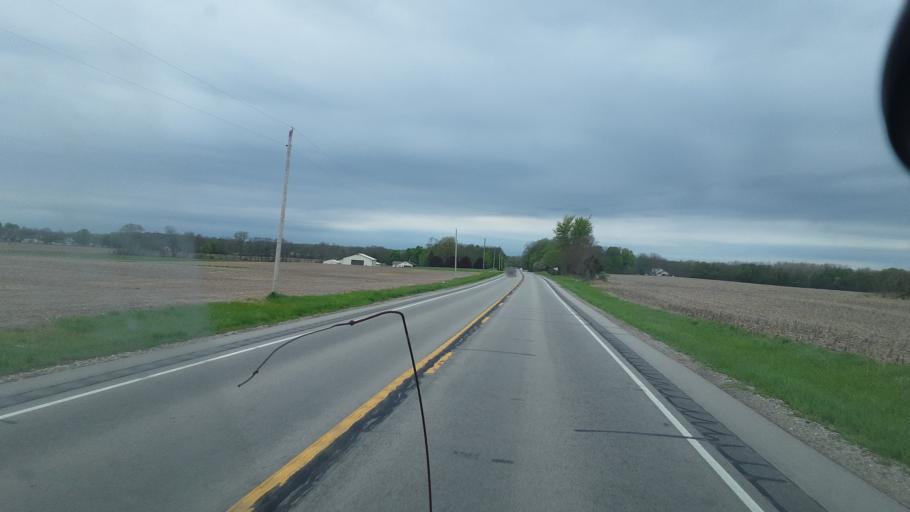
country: US
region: Indiana
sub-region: Kosciusko County
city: Syracuse
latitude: 41.5014
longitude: -85.7358
